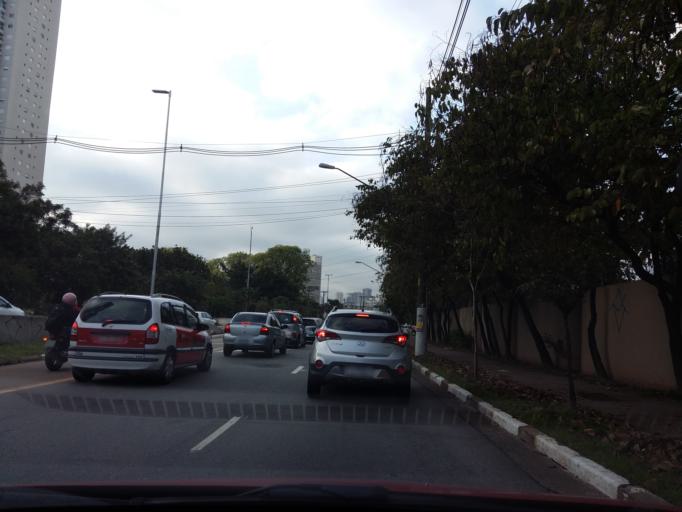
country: BR
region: Sao Paulo
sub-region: Sao Paulo
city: Sao Paulo
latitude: -23.5985
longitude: -46.6912
